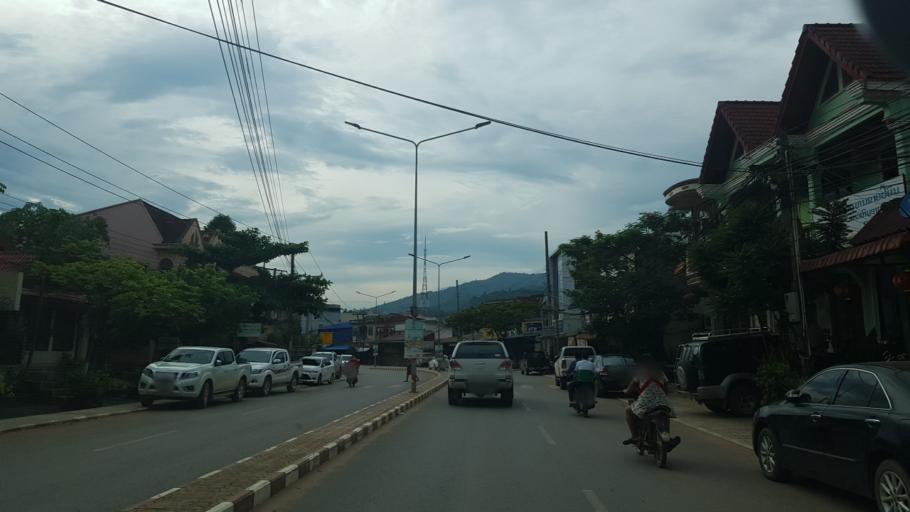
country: LA
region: Oudomxai
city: Muang Xay
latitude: 20.6874
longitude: 101.9869
